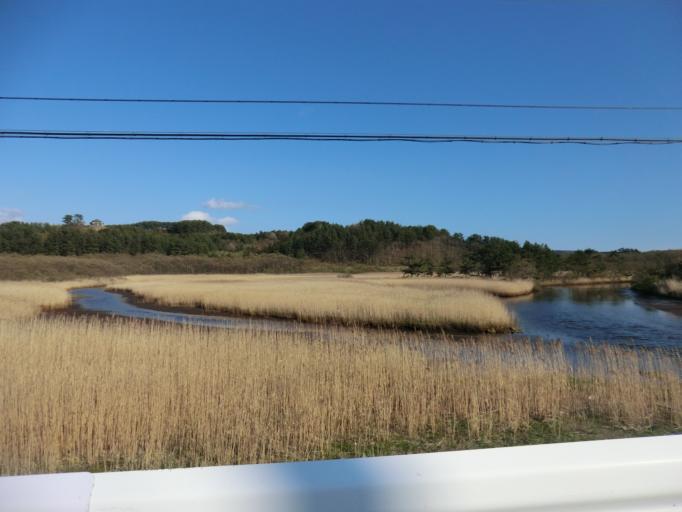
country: JP
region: Aomori
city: Mutsu
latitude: 41.3613
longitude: 141.3591
